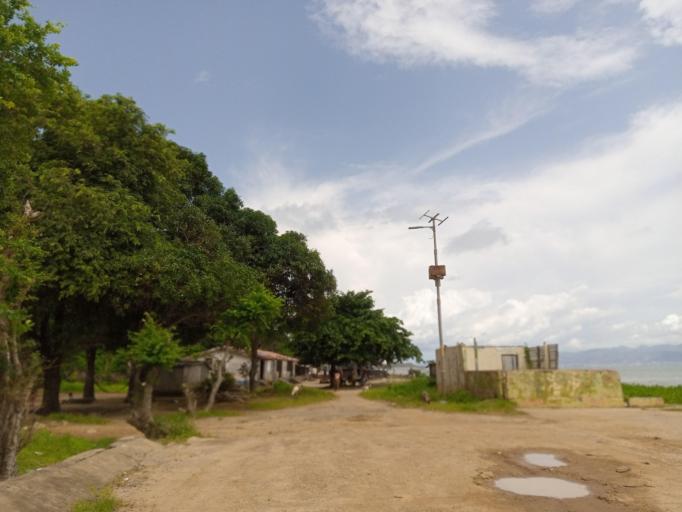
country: SL
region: Northern Province
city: Tintafor
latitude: 8.6184
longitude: -13.2127
